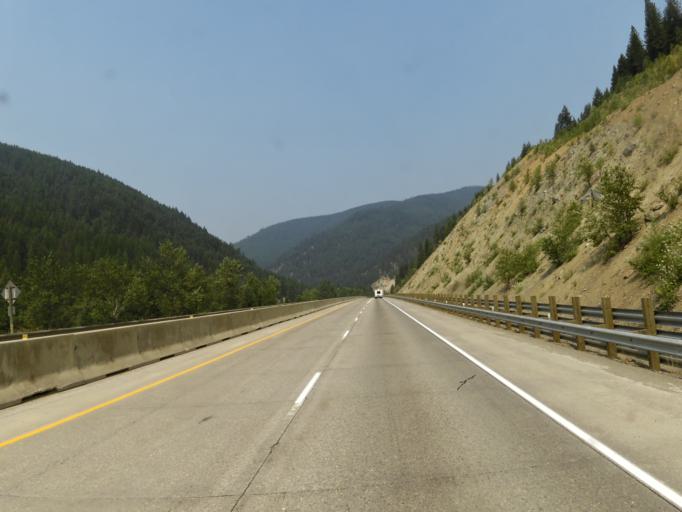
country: US
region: Montana
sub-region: Sanders County
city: Thompson Falls
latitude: 47.3046
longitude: -115.2033
